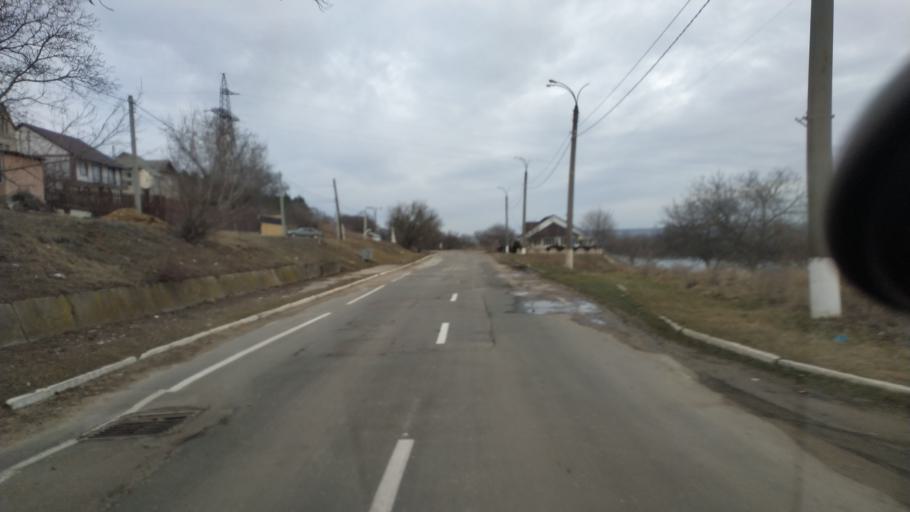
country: MD
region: Criuleni
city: Criuleni
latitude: 47.2232
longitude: 29.1630
